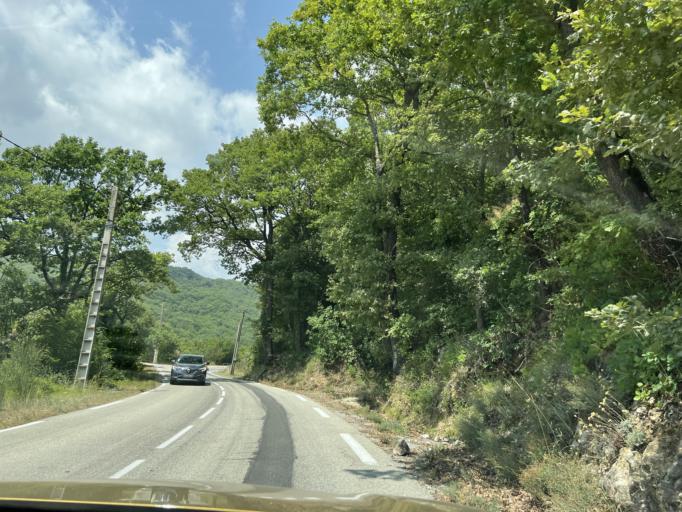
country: FR
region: Provence-Alpes-Cote d'Azur
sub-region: Departement des Alpes-Maritimes
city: Tourrettes-sur-Loup
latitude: 43.7752
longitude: 6.9822
